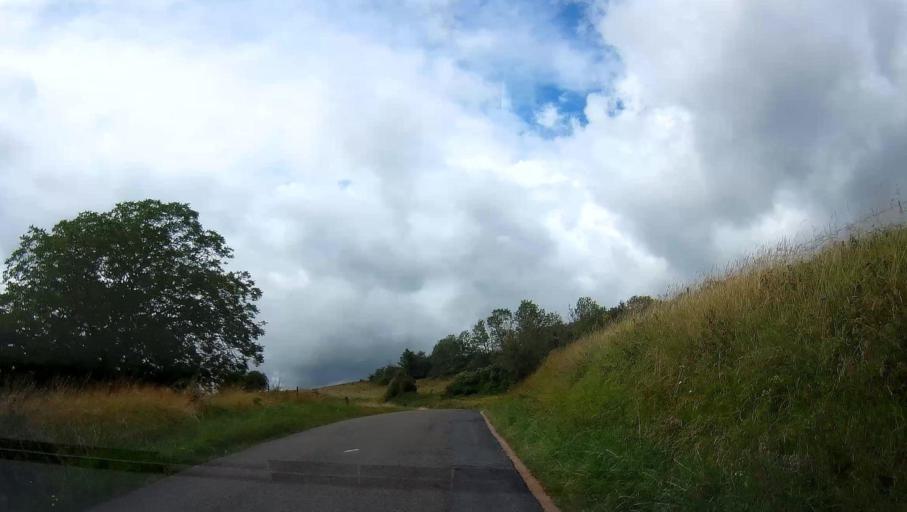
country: FR
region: Champagne-Ardenne
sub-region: Departement des Ardennes
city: Tournes
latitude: 49.7445
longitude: 4.5936
